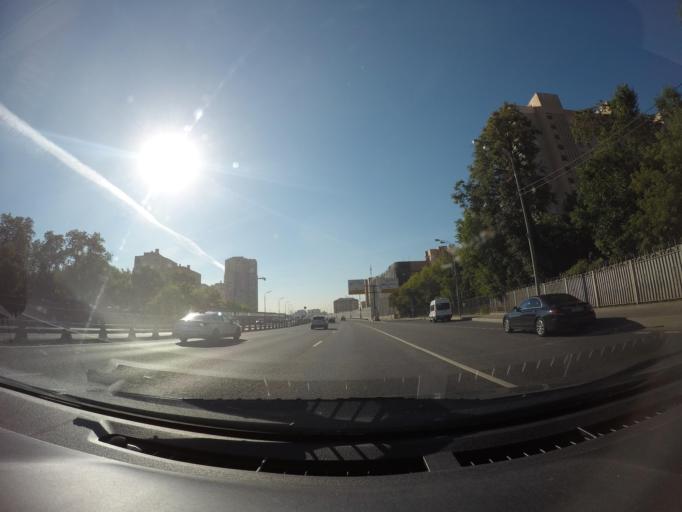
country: RU
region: Moscow
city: Sokol'niki
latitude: 55.7834
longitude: 37.6659
